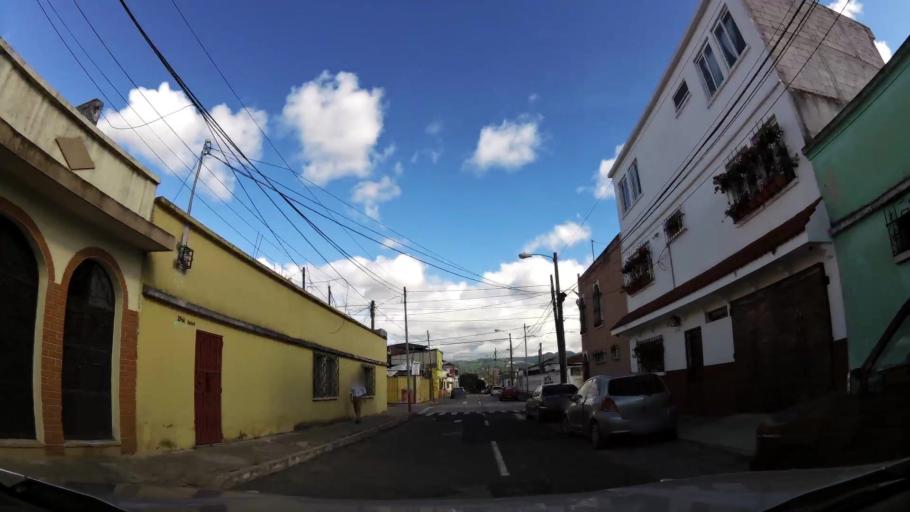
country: GT
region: Guatemala
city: Guatemala City
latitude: 14.6162
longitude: -90.5033
